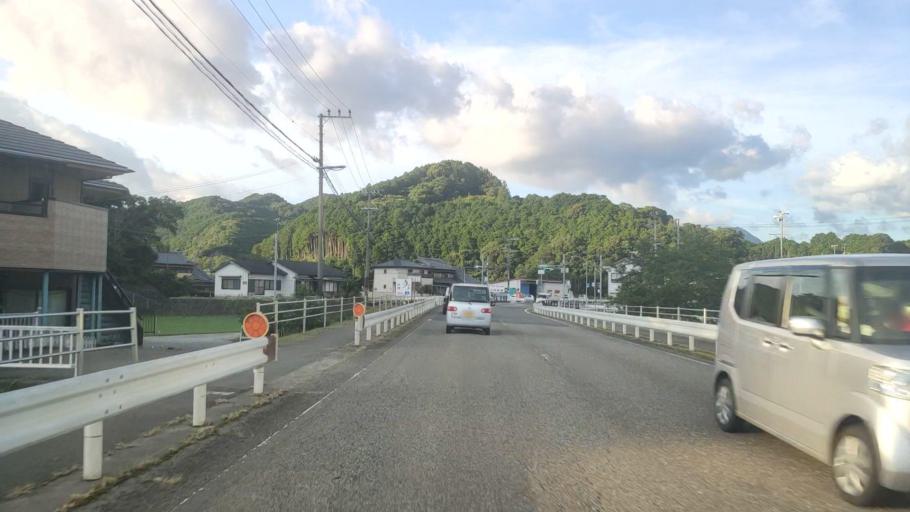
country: JP
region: Wakayama
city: Tanabe
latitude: 33.7178
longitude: 135.4717
